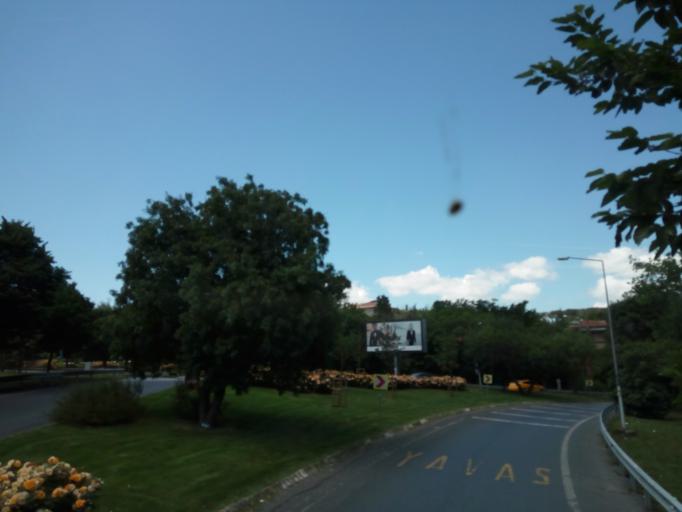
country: TR
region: Istanbul
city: UEskuedar
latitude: 41.0327
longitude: 29.0435
